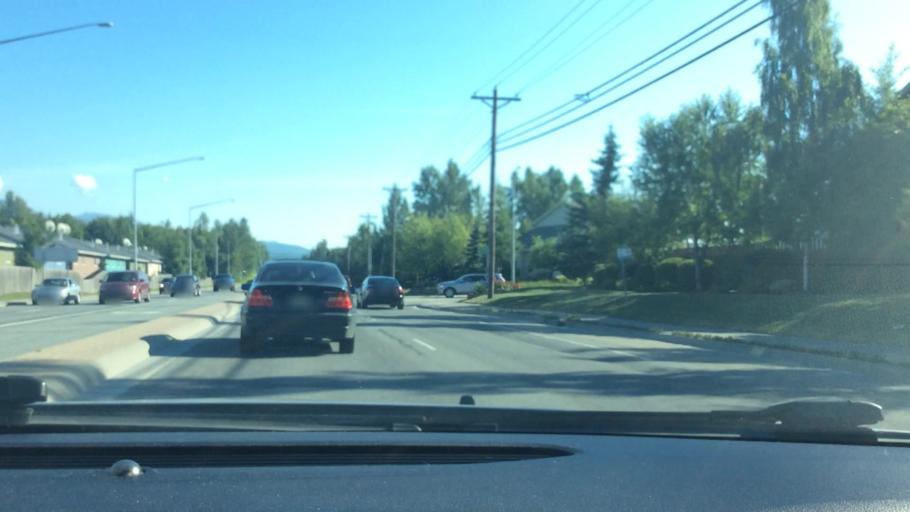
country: US
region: Alaska
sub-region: Anchorage Municipality
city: Elmendorf Air Force Base
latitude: 61.2000
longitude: -149.7335
